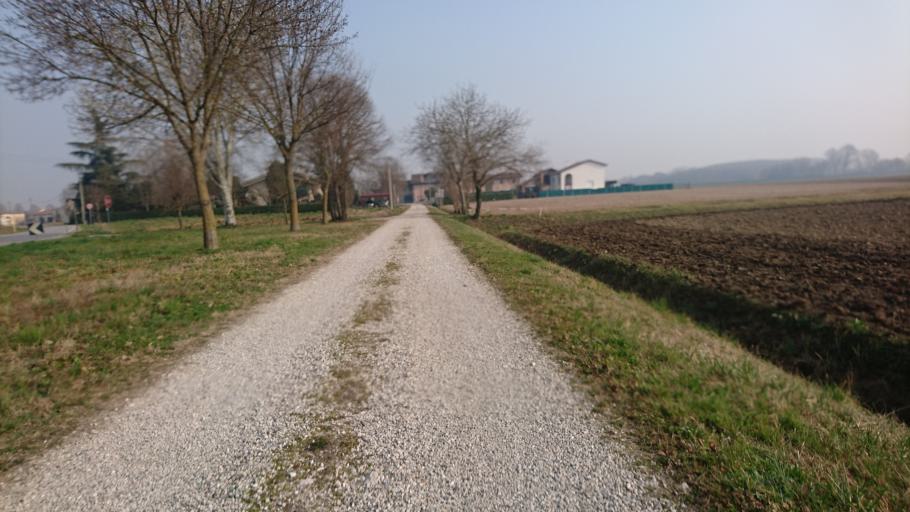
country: IT
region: Veneto
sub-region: Provincia di Padova
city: Veggiano
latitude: 45.4348
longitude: 11.7146
